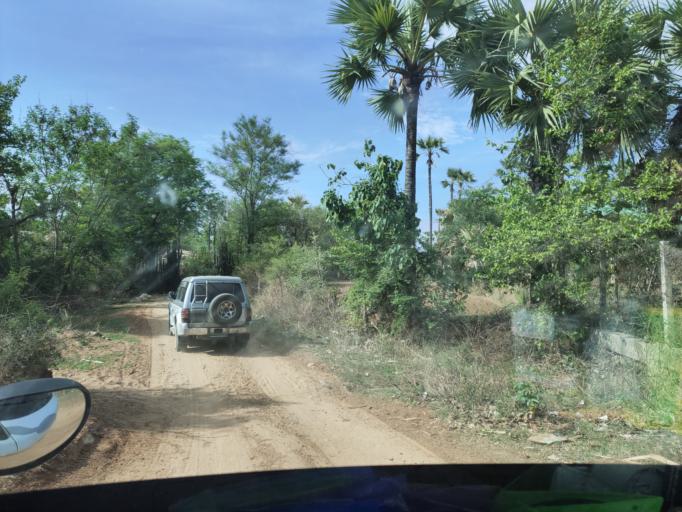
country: MM
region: Magway
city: Chauk
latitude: 20.9582
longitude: 94.9906
